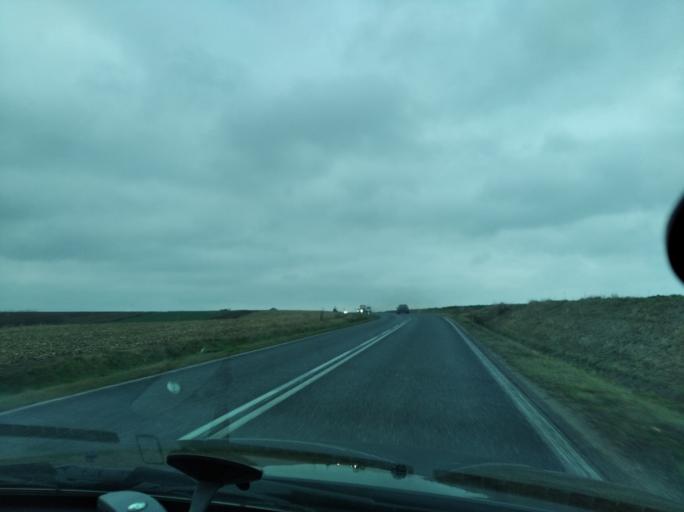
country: PL
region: Subcarpathian Voivodeship
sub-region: Powiat przeworski
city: Kanczuga
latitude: 49.9921
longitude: 22.3826
